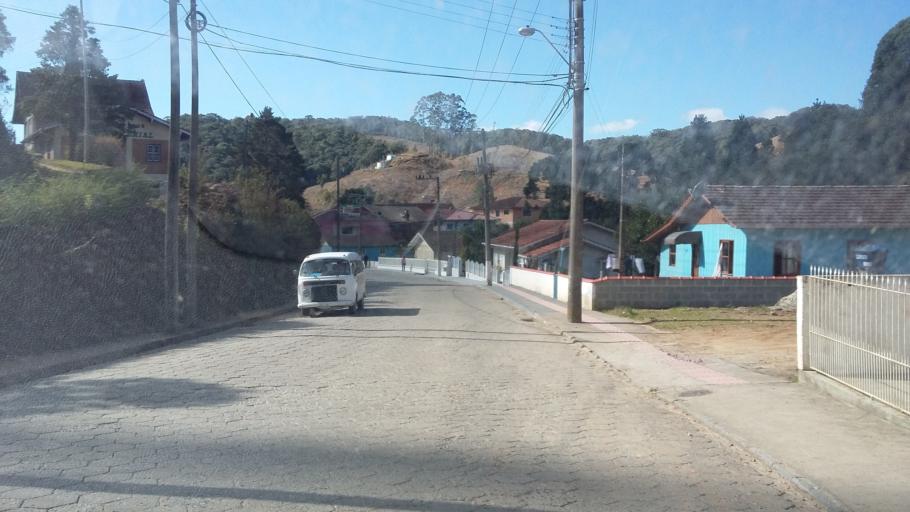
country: BR
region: Santa Catarina
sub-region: Santo Amaro Da Imperatriz
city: Santo Amaro da Imperatriz
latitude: -27.6741
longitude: -49.0148
